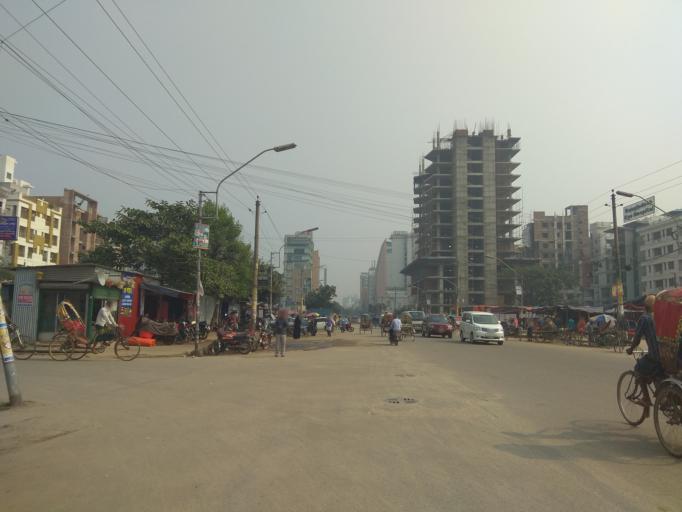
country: BD
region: Dhaka
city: Tungi
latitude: 23.8741
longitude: 90.3872
